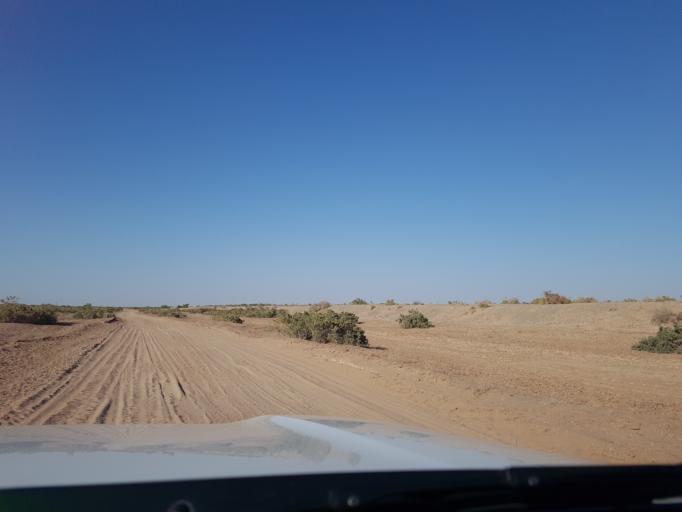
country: IR
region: Razavi Khorasan
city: Sarakhs
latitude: 36.9877
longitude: 61.3873
